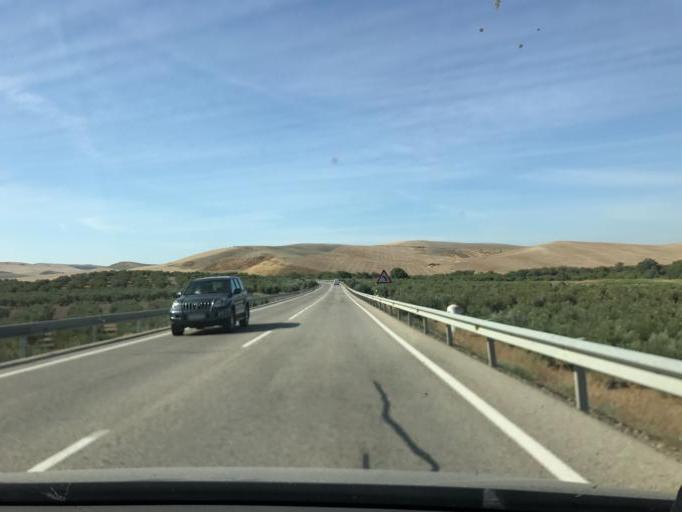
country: ES
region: Andalusia
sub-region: Province of Cordoba
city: Espejo
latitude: 37.7291
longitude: -4.6360
